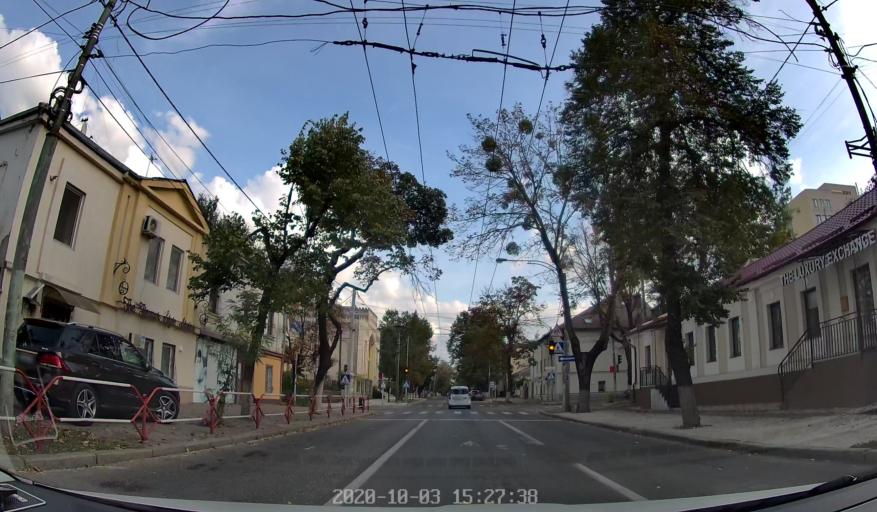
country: MD
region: Chisinau
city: Chisinau
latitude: 47.0237
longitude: 28.8189
